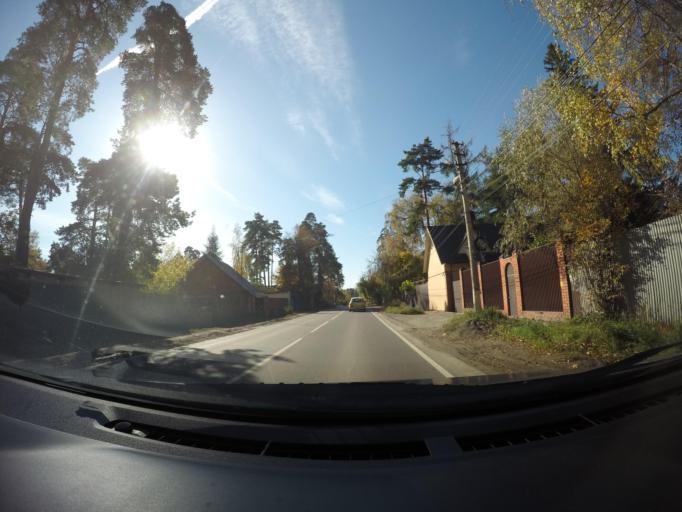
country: RU
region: Moskovskaya
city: Rodniki
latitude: 55.6356
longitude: 38.0516
